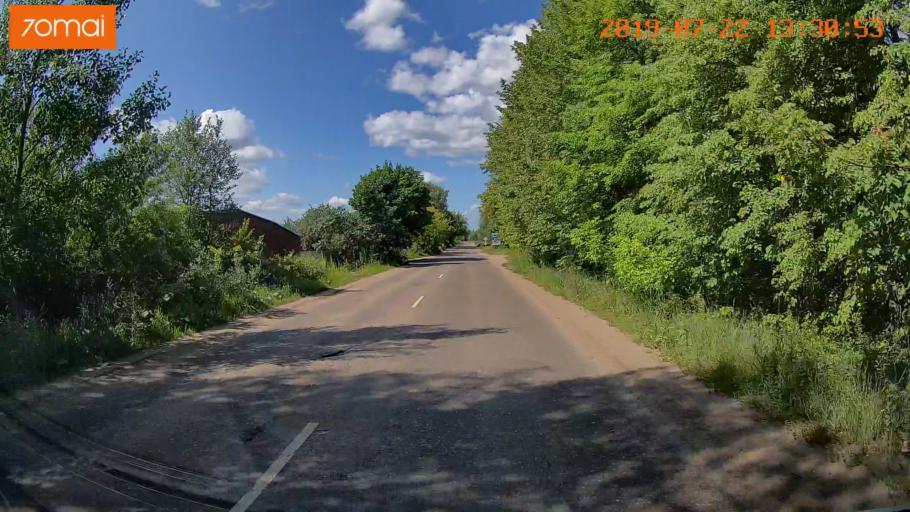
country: RU
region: Ivanovo
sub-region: Gorod Ivanovo
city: Ivanovo
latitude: 57.0547
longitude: 40.9230
